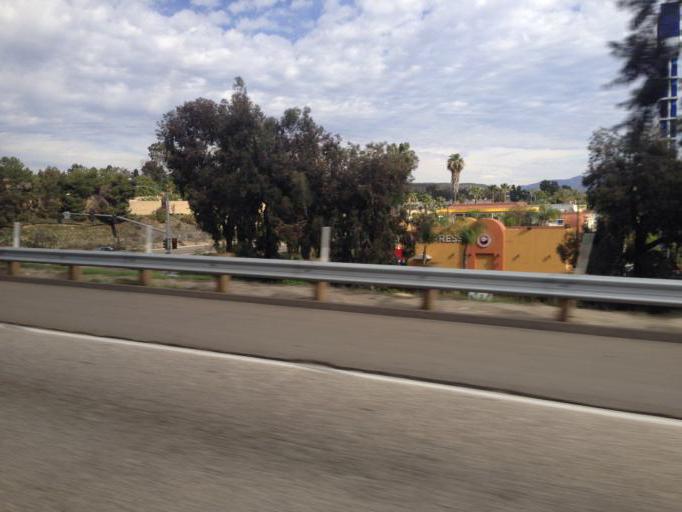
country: US
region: California
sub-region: San Diego County
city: Bonita
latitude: 32.5942
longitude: -117.0362
